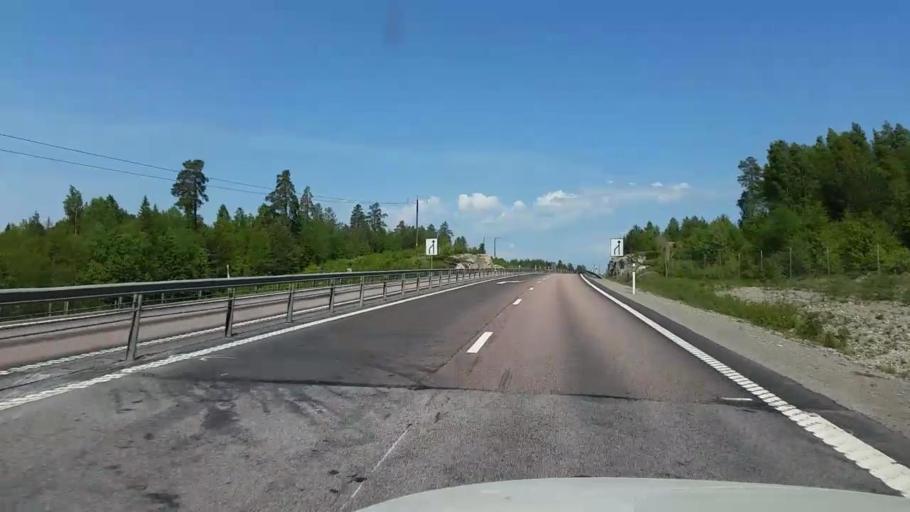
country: SE
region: Gaevleborg
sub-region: Hudiksvalls Kommun
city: Hudiksvall
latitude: 61.7303
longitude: 17.0656
